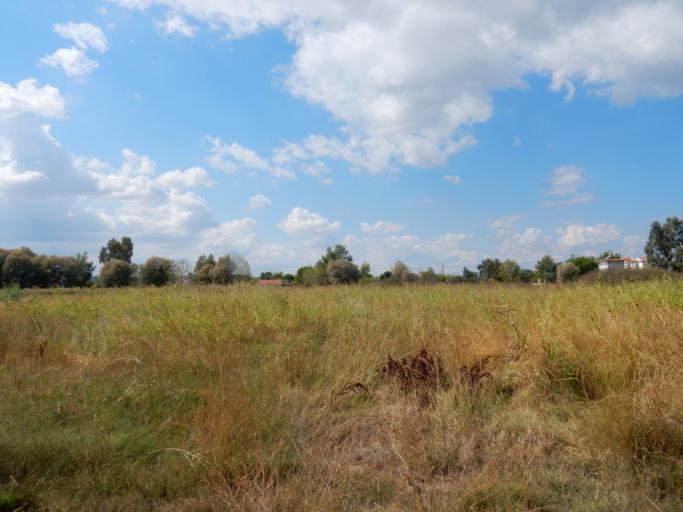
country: GR
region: Attica
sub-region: Nomarchia Anatolikis Attikis
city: Skala Oropou
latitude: 38.3331
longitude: 23.7663
